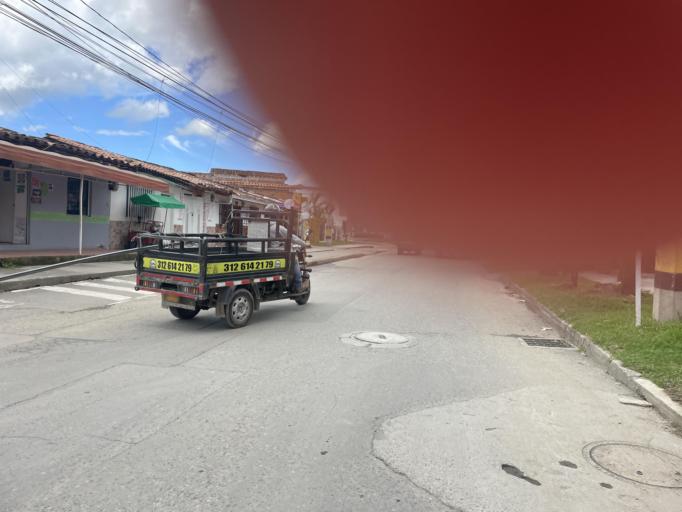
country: CO
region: Antioquia
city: La Ceja
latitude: 6.0233
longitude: -75.4326
